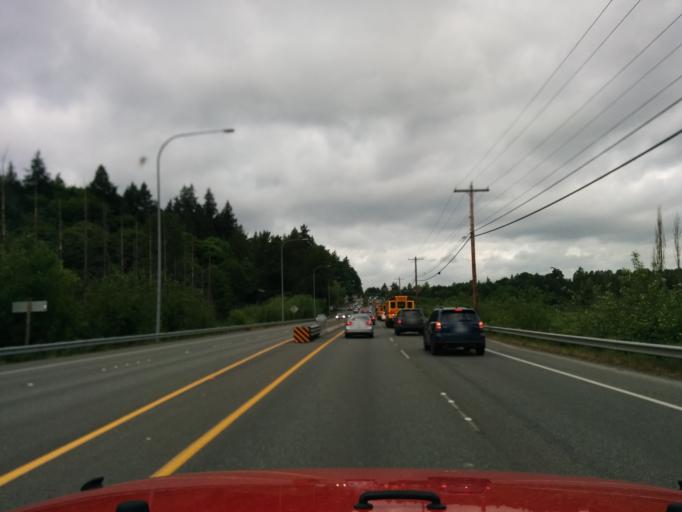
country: US
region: Washington
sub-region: King County
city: Sammamish
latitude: 47.6560
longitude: -122.0801
